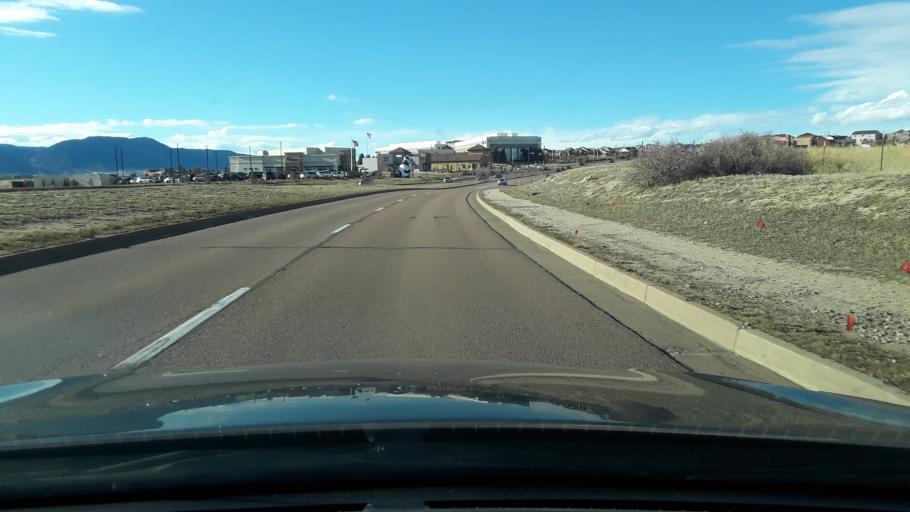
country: US
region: Colorado
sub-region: El Paso County
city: Gleneagle
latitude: 39.0222
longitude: -104.8156
